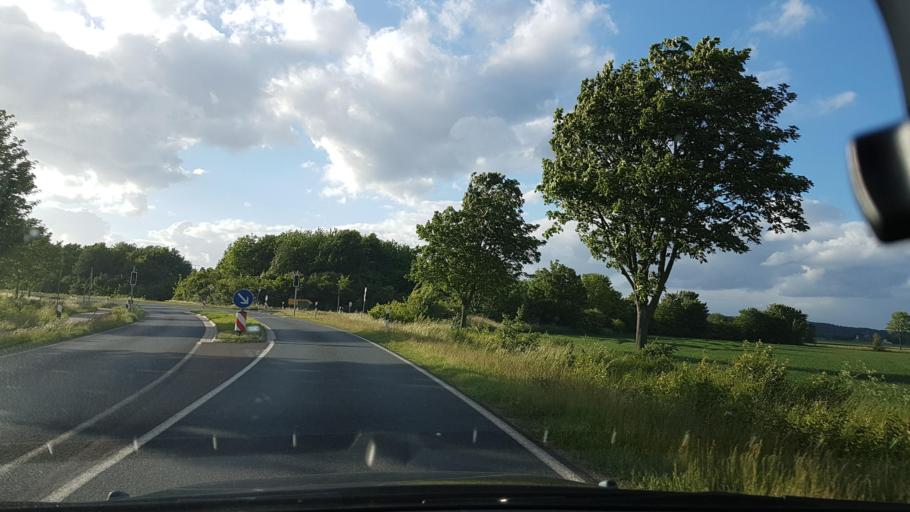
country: DE
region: Lower Saxony
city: Gehrden
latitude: 52.3151
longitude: 9.6218
